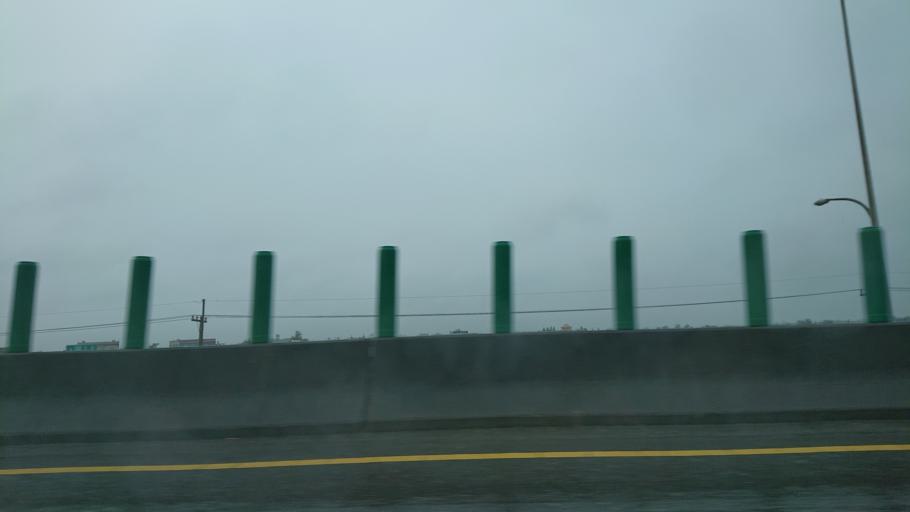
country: TW
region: Taiwan
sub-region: Chiayi
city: Taibao
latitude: 23.7302
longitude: 120.2245
